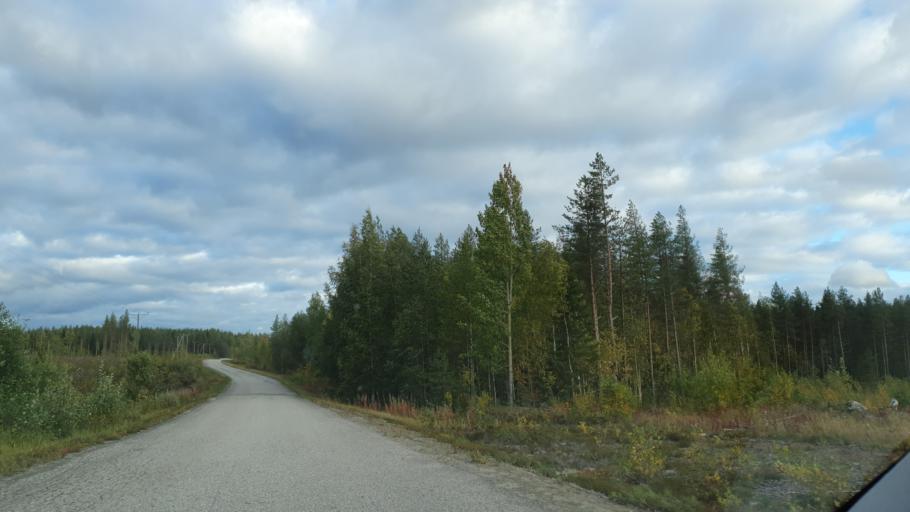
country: FI
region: North Karelia
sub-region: Pielisen Karjala
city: Lieksa
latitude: 63.9159
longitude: 30.1746
